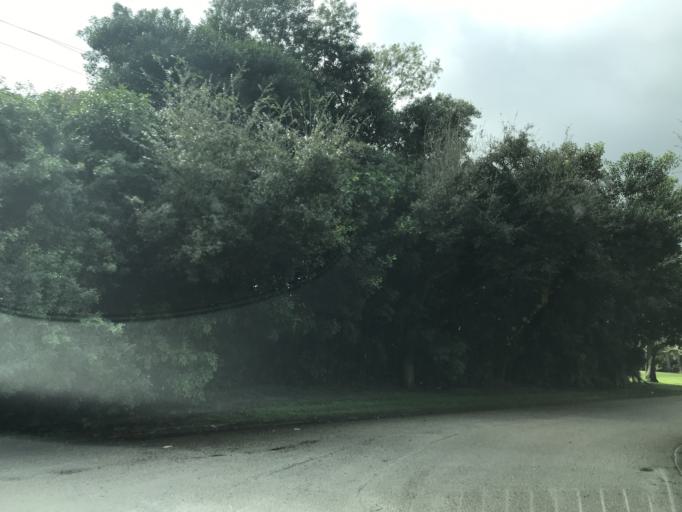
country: US
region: Florida
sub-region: Palm Beach County
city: Delray Beach
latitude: 26.4518
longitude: -80.0938
